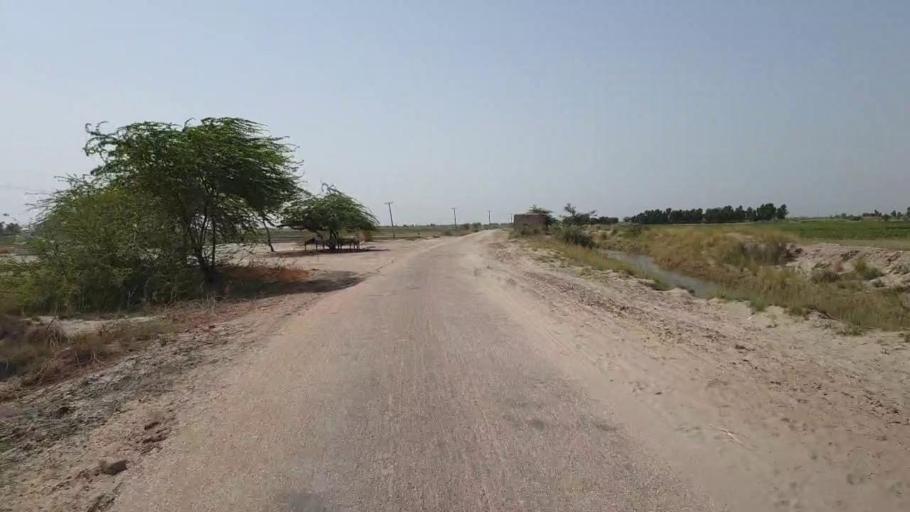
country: PK
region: Sindh
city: Jam Sahib
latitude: 26.4169
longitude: 68.9088
